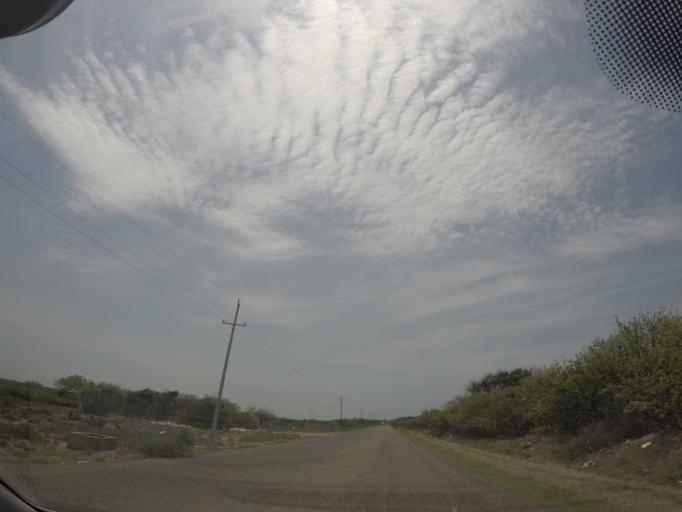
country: MX
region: Oaxaca
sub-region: San Mateo del Mar
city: Colonia Juarez
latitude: 16.2132
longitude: -95.0550
